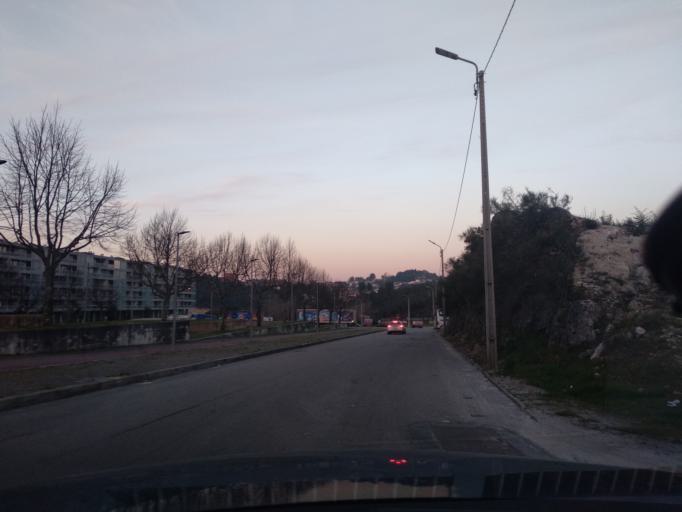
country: PT
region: Porto
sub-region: Paredes
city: Lordelo
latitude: 41.2340
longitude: -8.4147
